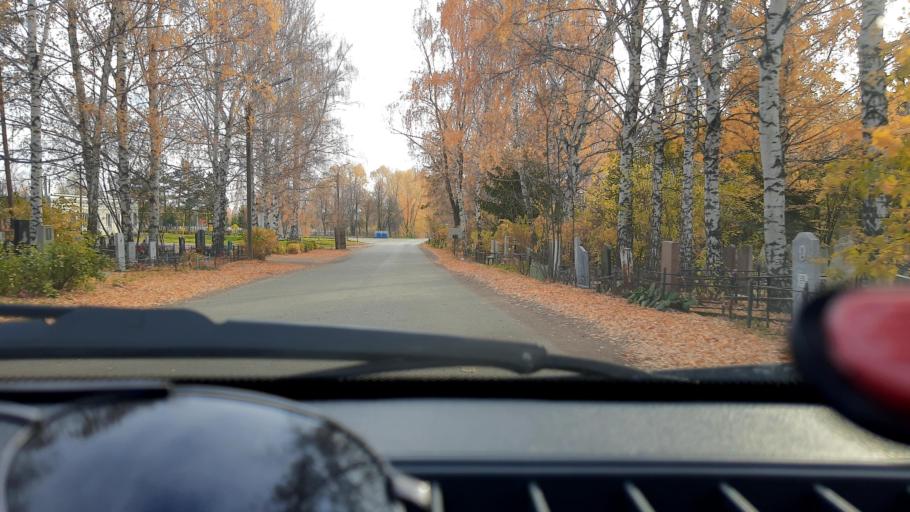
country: RU
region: Bashkortostan
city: Ufa
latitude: 54.8522
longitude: 56.1554
